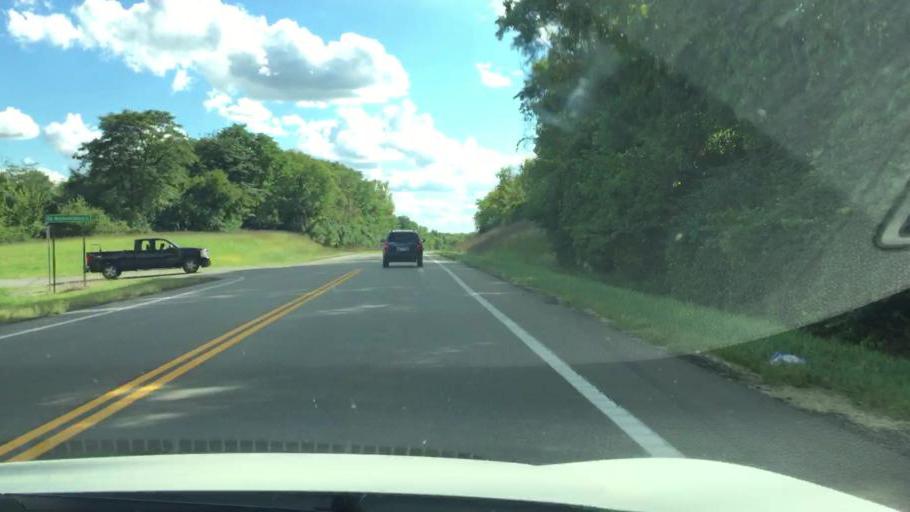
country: US
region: Ohio
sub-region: Clark County
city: Northridge
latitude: 39.9916
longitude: -83.7305
